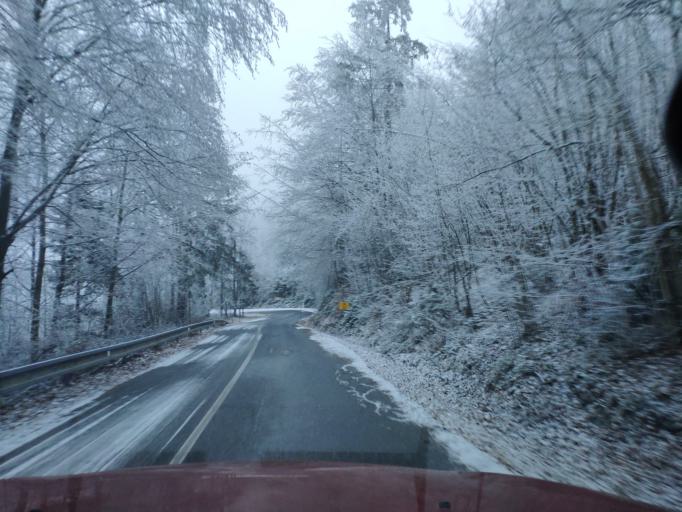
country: SK
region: Kosicky
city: Dobsina
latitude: 48.8125
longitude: 20.4844
